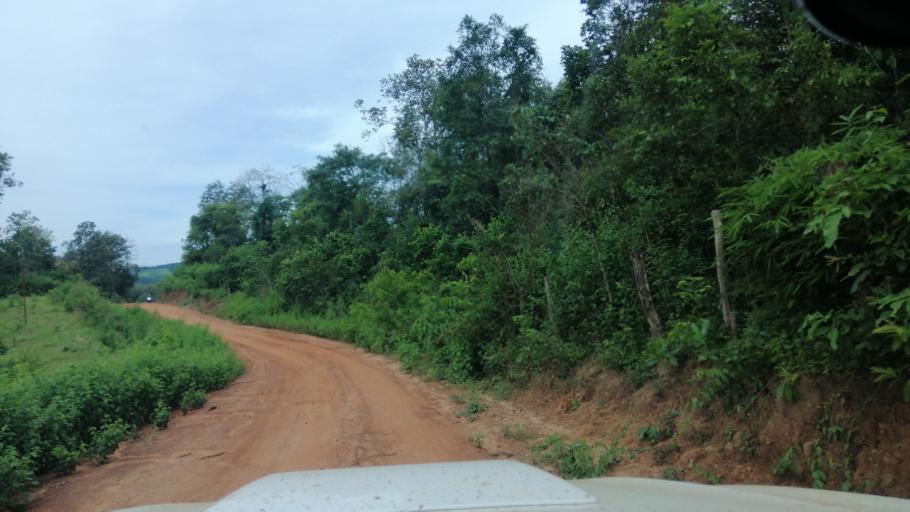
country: TH
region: Loei
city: Na Haeo
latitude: 17.5782
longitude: 101.1570
